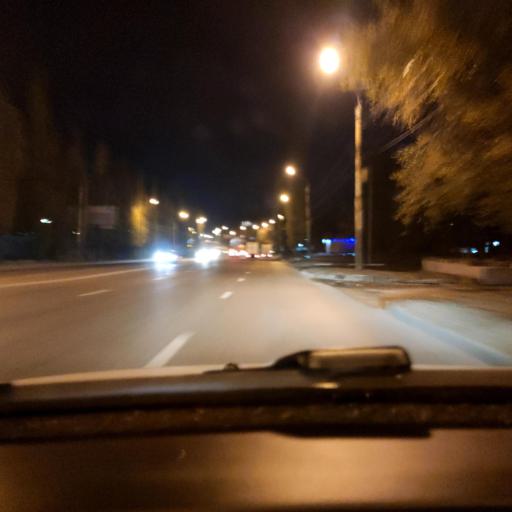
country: RU
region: Voronezj
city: Voronezh
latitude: 51.6258
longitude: 39.2318
